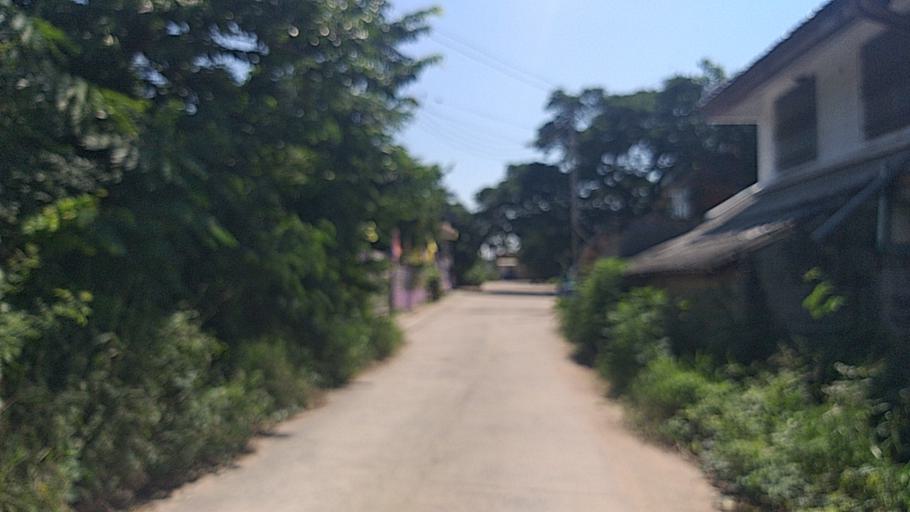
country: TH
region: Nakhon Ratchasima
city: Prathai
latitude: 15.5342
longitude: 102.7237
